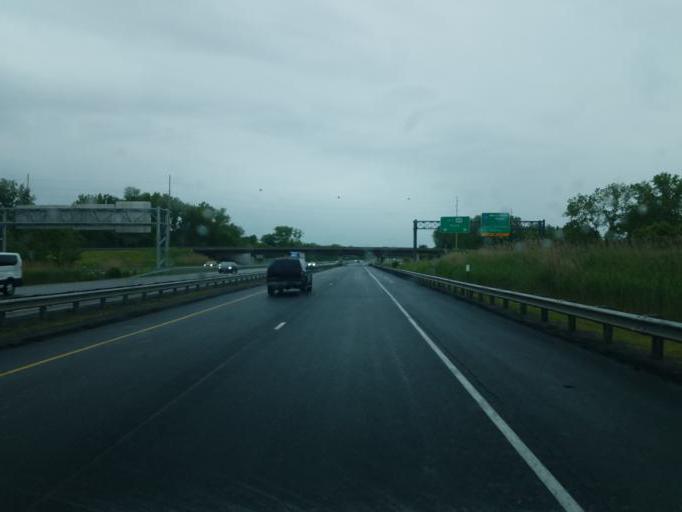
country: US
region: New York
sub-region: Oneida County
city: Utica
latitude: 43.1250
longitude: -75.2406
